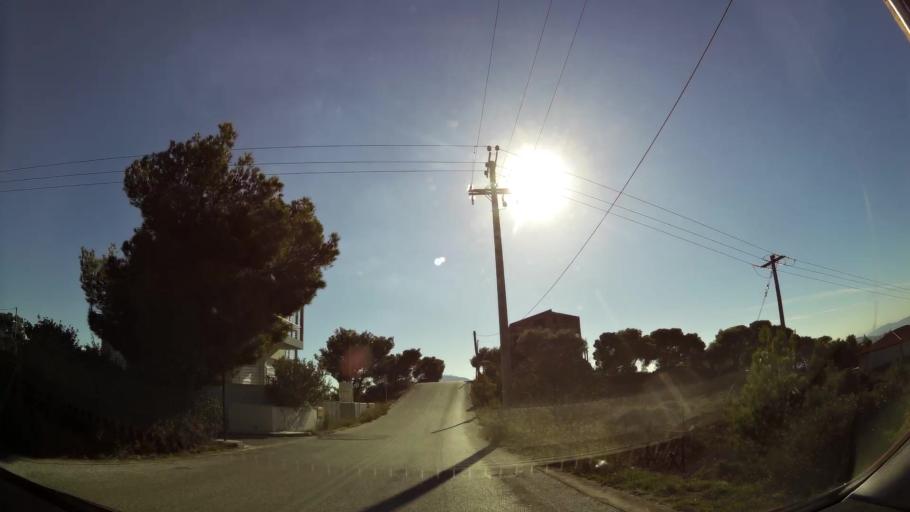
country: GR
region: Attica
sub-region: Nomarchia Anatolikis Attikis
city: Anthousa
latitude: 38.0331
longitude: 23.8737
